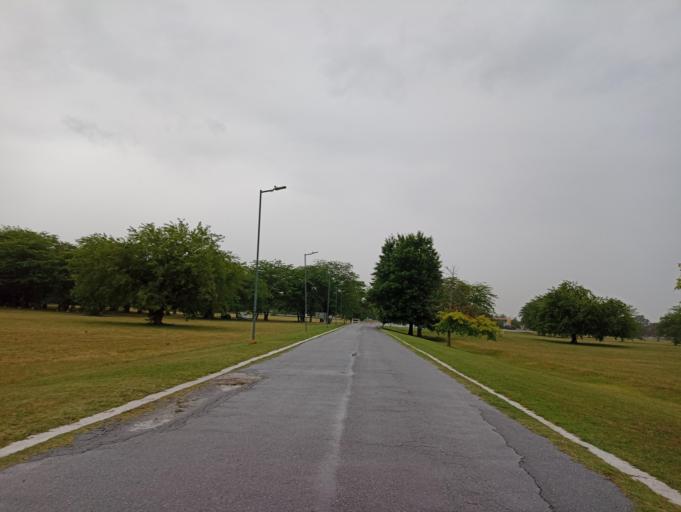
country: AR
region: Buenos Aires
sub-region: Partido de La Plata
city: La Plata
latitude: -34.8618
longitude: -58.0728
